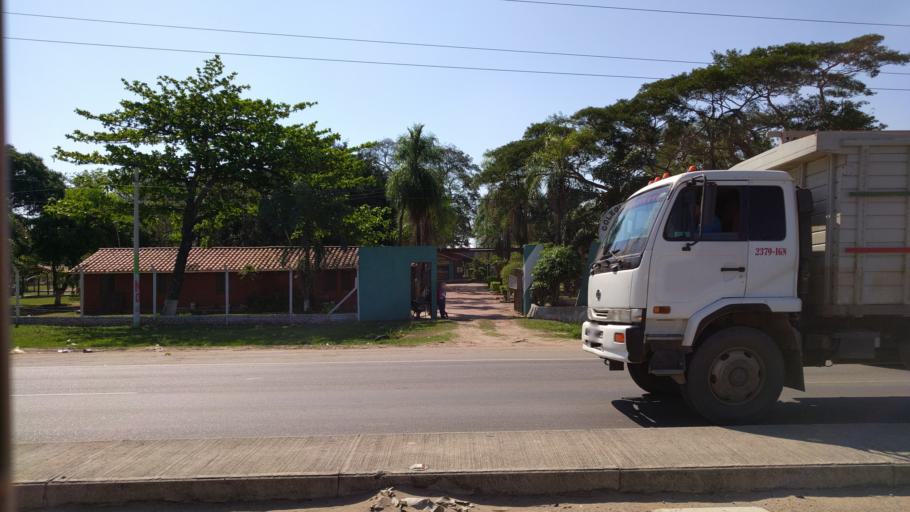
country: BO
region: Santa Cruz
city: Cotoca
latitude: -17.7592
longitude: -63.0136
